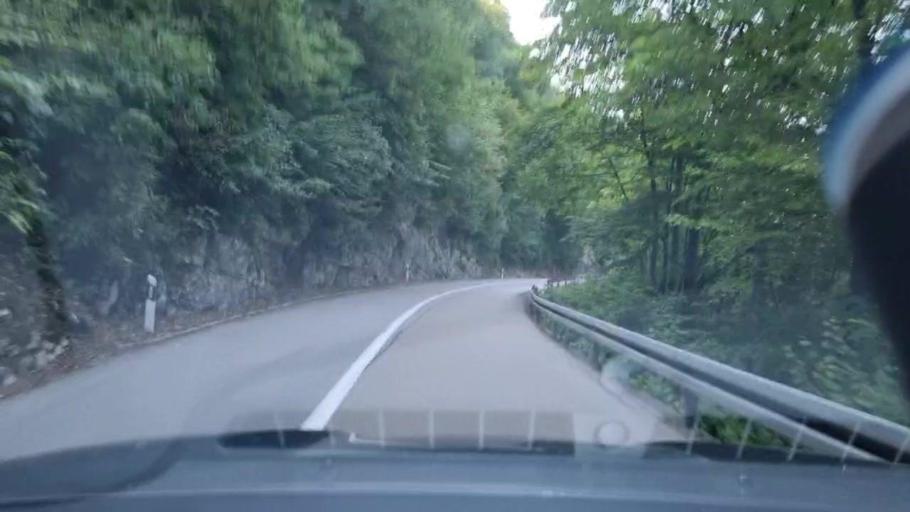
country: BA
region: Federation of Bosnia and Herzegovina
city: Stijena
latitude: 44.8914
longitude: 16.0498
